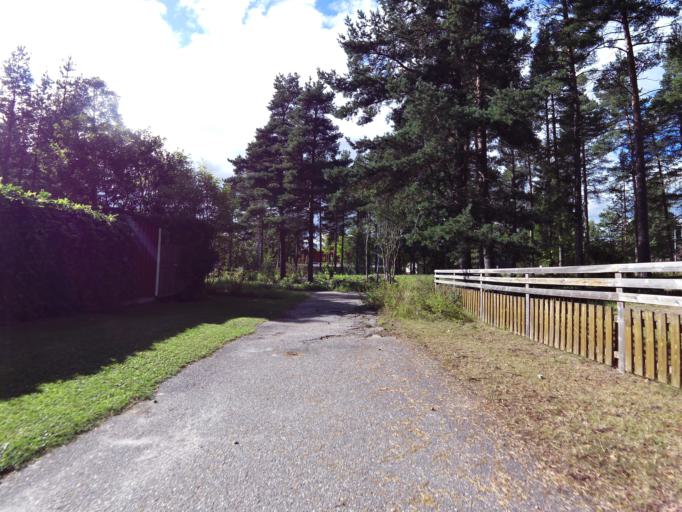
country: SE
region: Gaevleborg
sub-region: Gavle Kommun
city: Gavle
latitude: 60.6680
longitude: 17.2166
